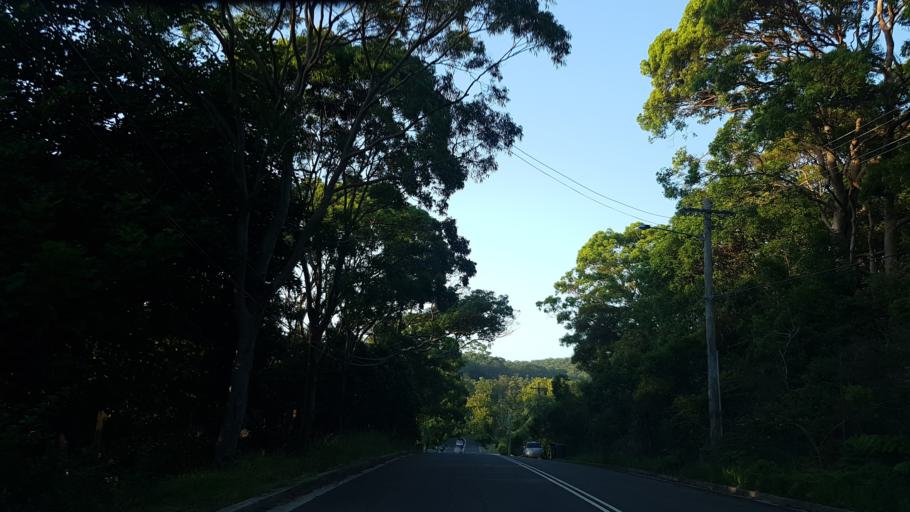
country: AU
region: New South Wales
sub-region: Warringah
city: Narraweena
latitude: -33.7389
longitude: 151.2697
